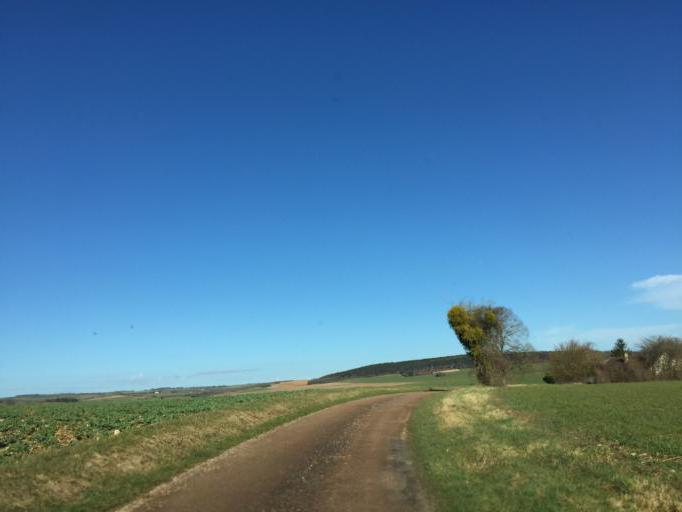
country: FR
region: Bourgogne
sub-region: Departement de l'Yonne
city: Fontenailles
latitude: 47.5553
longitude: 3.3270
